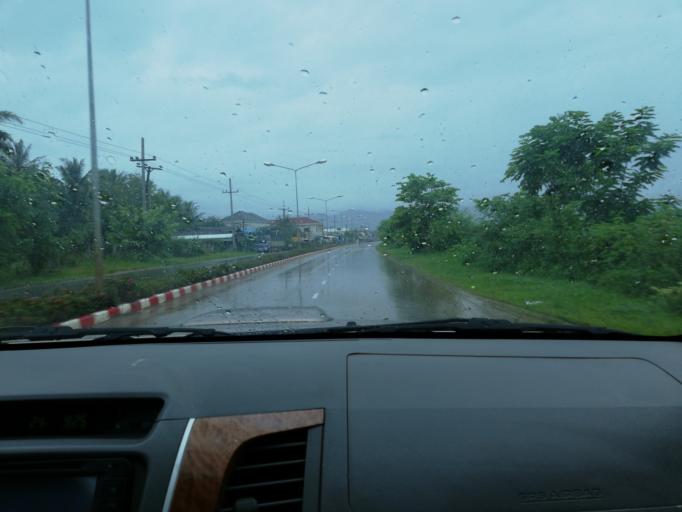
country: LA
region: Loungnamtha
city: Louang Namtha
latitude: 20.9553
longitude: 101.4039
